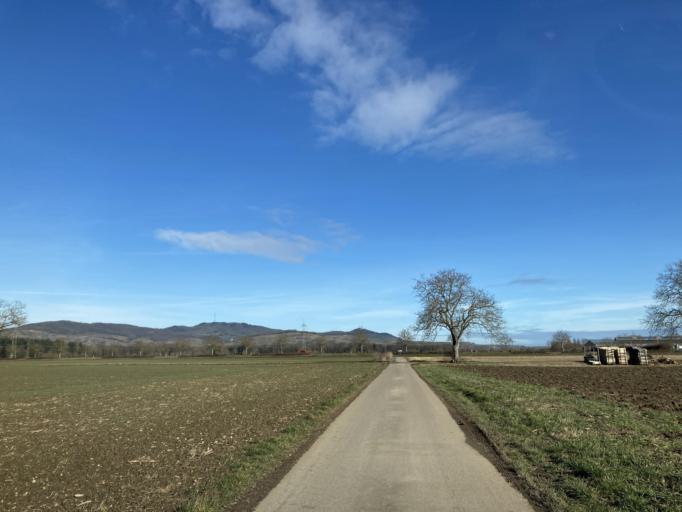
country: DE
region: Baden-Wuerttemberg
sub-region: Freiburg Region
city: Merdingen
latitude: 48.0202
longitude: 7.6744
